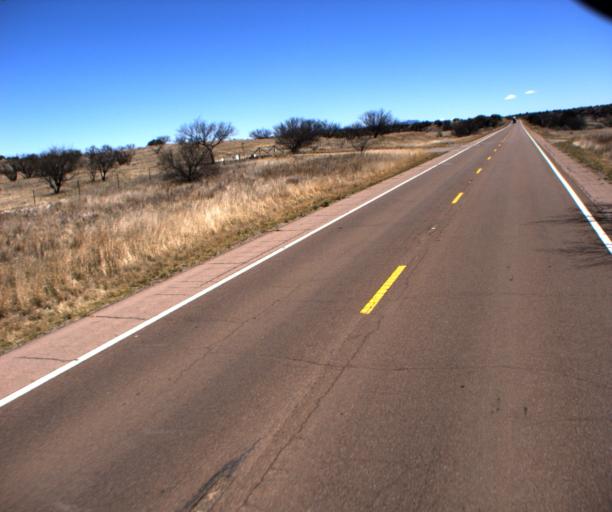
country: US
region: Arizona
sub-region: Pima County
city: Corona de Tucson
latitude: 31.6590
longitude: -110.6953
